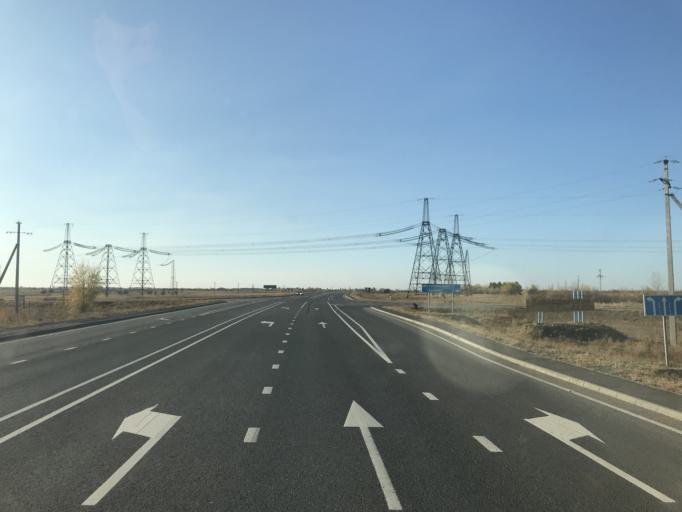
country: KZ
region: Pavlodar
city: Koktobe
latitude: 51.9086
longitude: 77.3603
